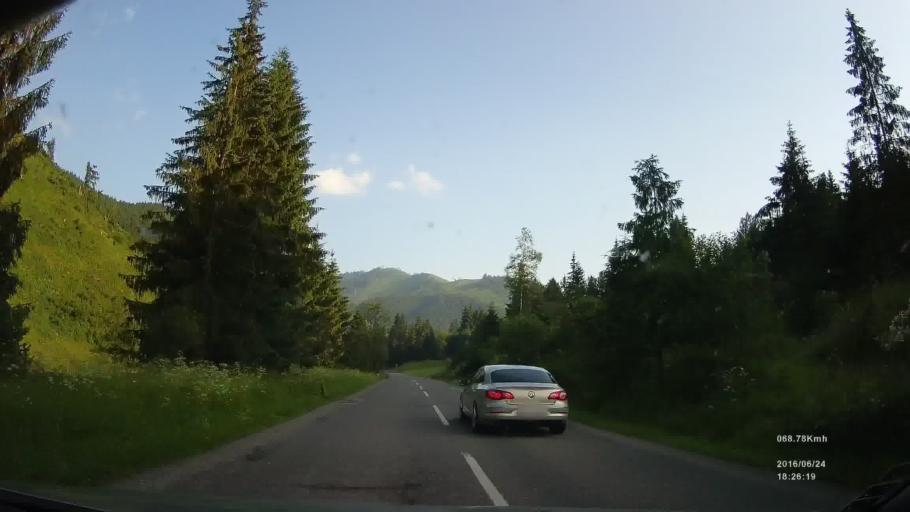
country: SK
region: Zilinsky
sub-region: Okres Zilina
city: Liptovsky Hradok
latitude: 48.9592
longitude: 19.7736
